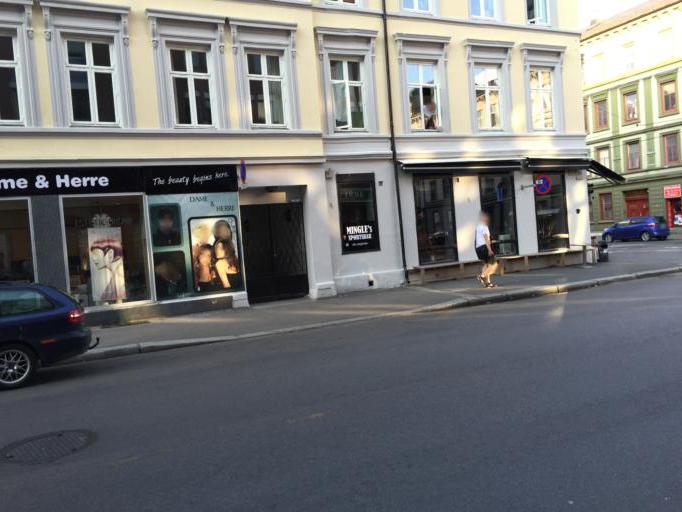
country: NO
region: Oslo
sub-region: Oslo
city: Oslo
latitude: 59.9192
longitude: 10.7623
